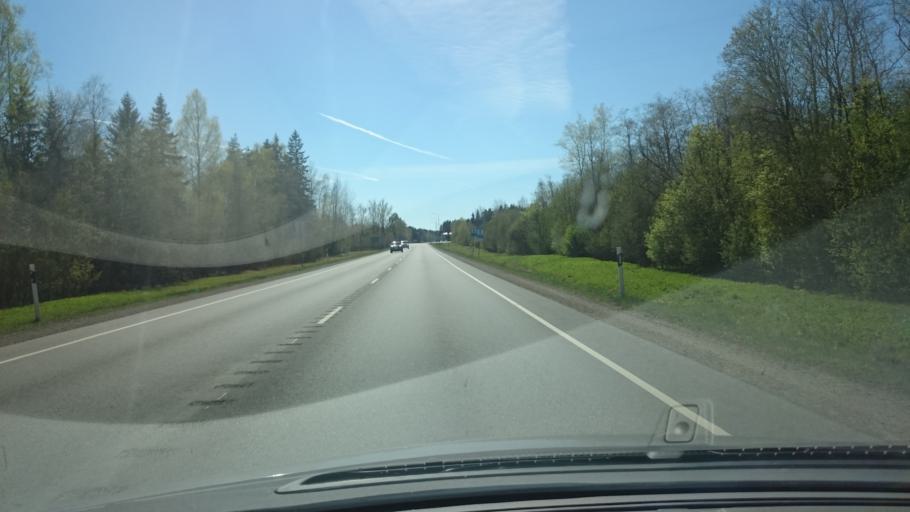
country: EE
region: Ida-Virumaa
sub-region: Johvi vald
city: Johvi
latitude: 59.3656
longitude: 27.4719
